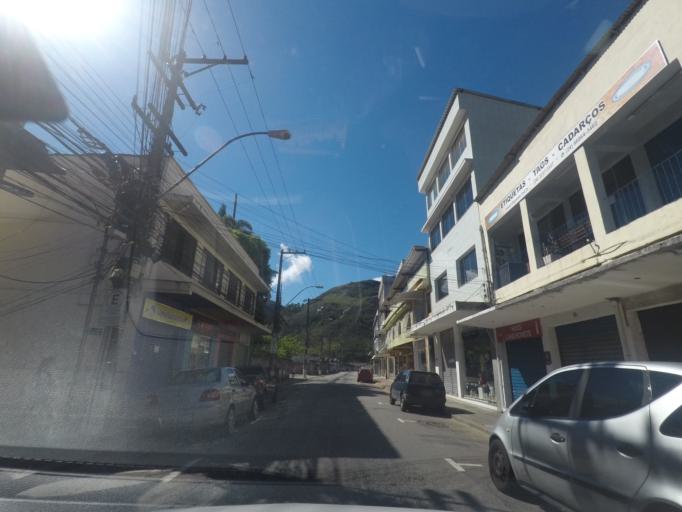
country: BR
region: Rio de Janeiro
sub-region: Petropolis
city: Petropolis
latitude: -22.5170
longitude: -43.1703
